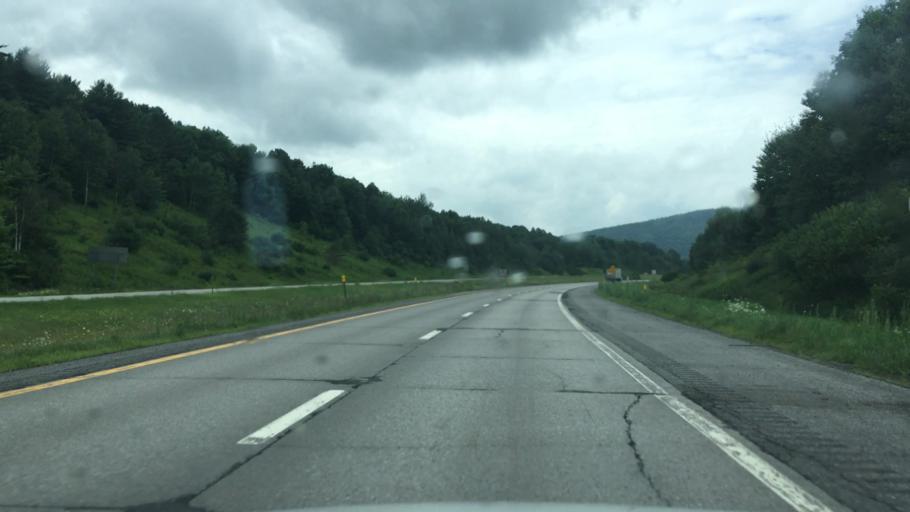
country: US
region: New York
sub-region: Otsego County
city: Worcester
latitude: 42.5883
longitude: -74.7379
